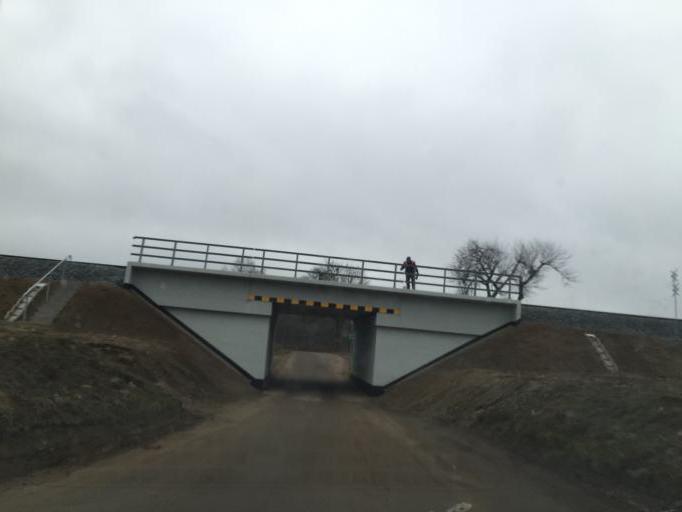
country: PL
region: Pomeranian Voivodeship
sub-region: Powiat kartuski
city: Banino
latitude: 54.4048
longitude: 18.4403
